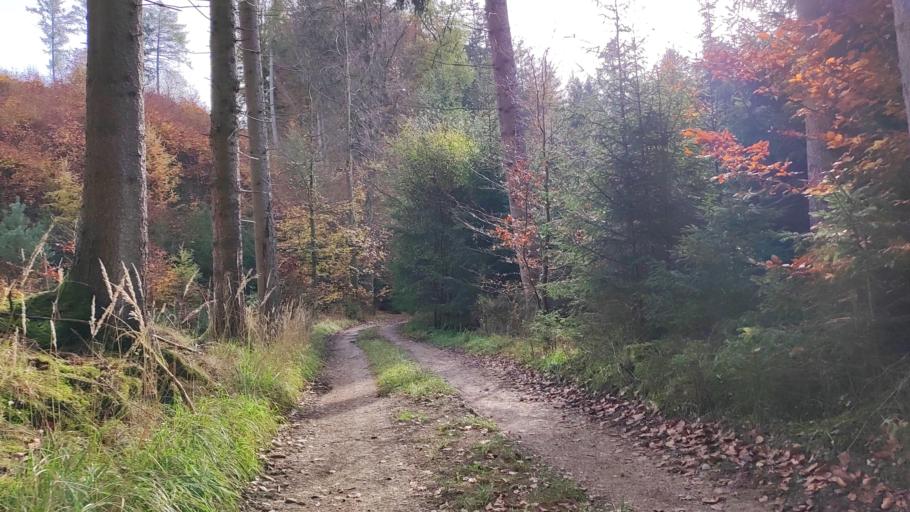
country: DE
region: Bavaria
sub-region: Swabia
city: Langenneufnach
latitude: 48.2924
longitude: 10.5965
